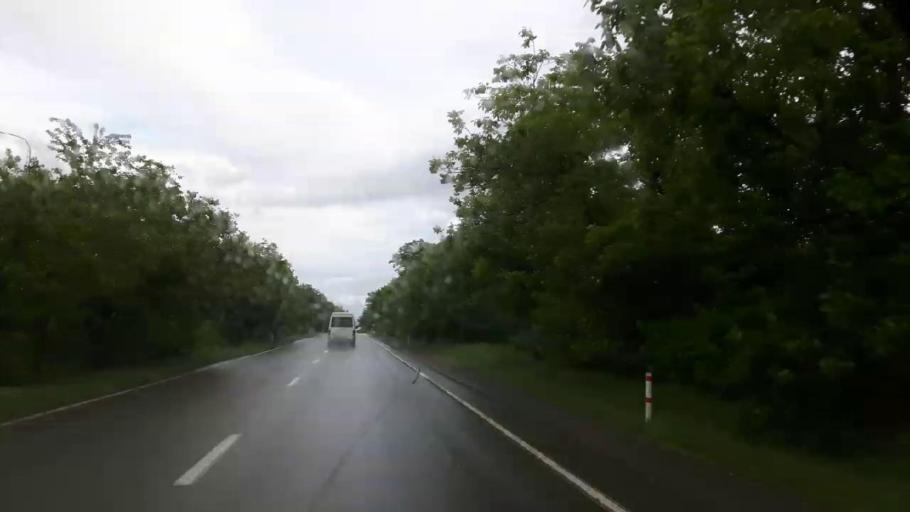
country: GE
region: Shida Kartli
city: Kaspi
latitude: 41.9595
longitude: 44.4811
